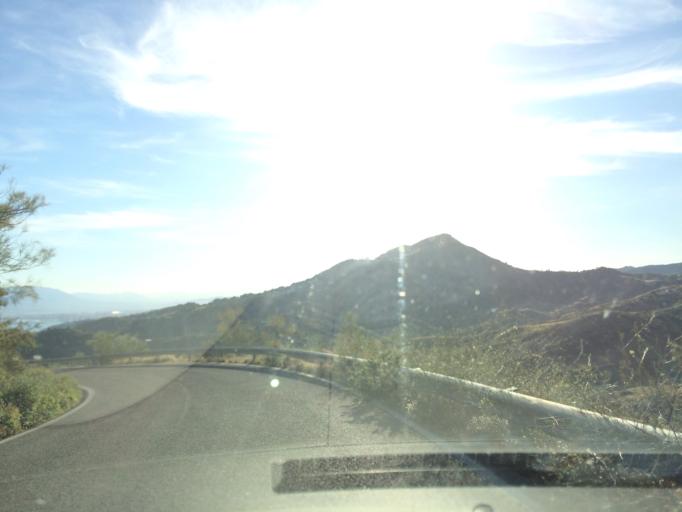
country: ES
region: Andalusia
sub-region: Provincia de Malaga
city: Totalan
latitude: 36.7406
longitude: -4.3312
